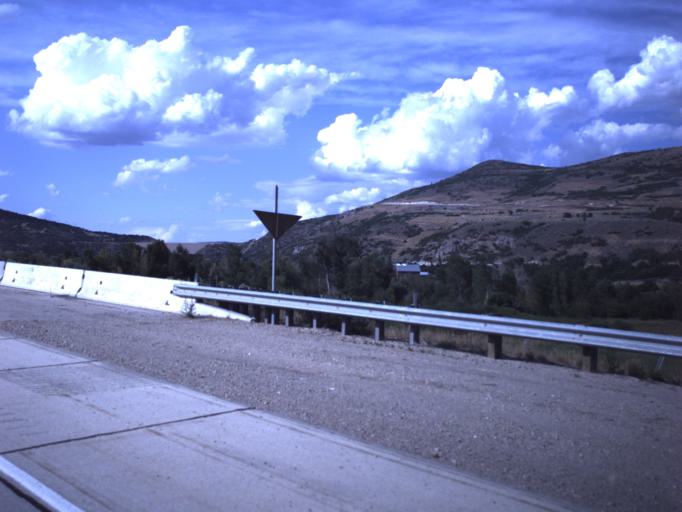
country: US
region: Utah
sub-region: Wasatch County
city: Heber
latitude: 40.5694
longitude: -111.4304
